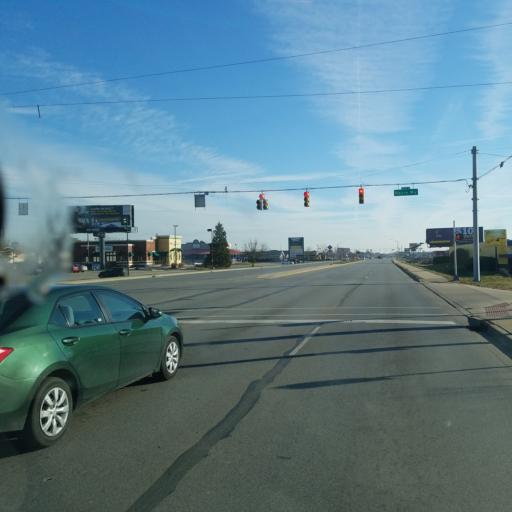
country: US
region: Indiana
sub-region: Marion County
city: Speedway
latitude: 39.8238
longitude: -86.2499
